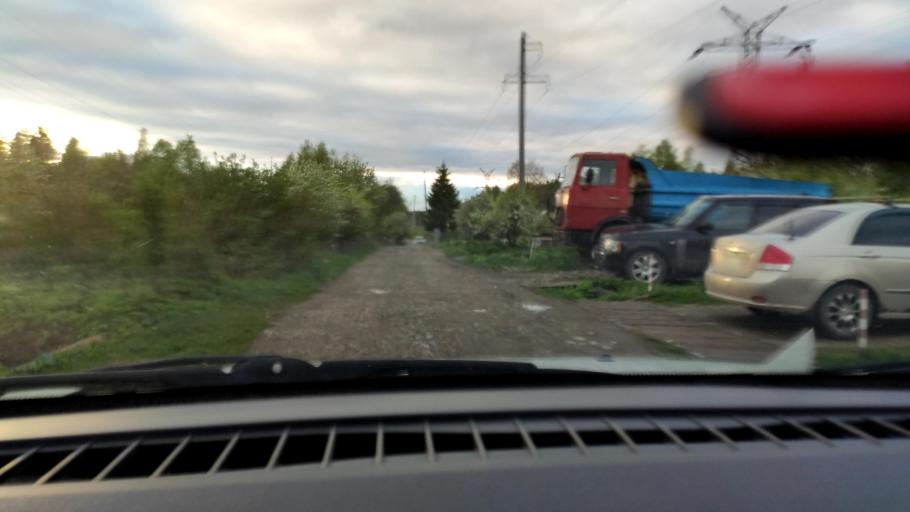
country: RU
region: Perm
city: Polazna
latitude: 58.1324
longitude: 56.4109
